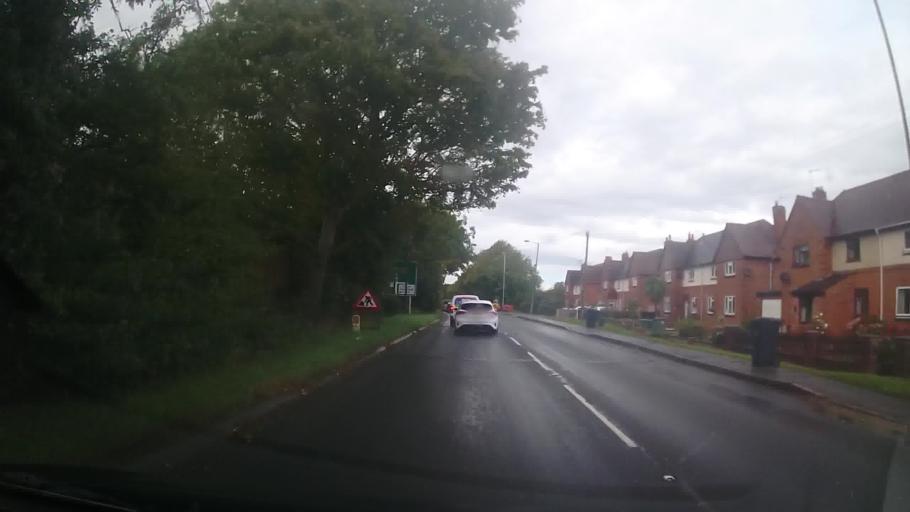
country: GB
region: England
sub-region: Worcestershire
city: Pershore
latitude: 52.1323
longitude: -2.0679
